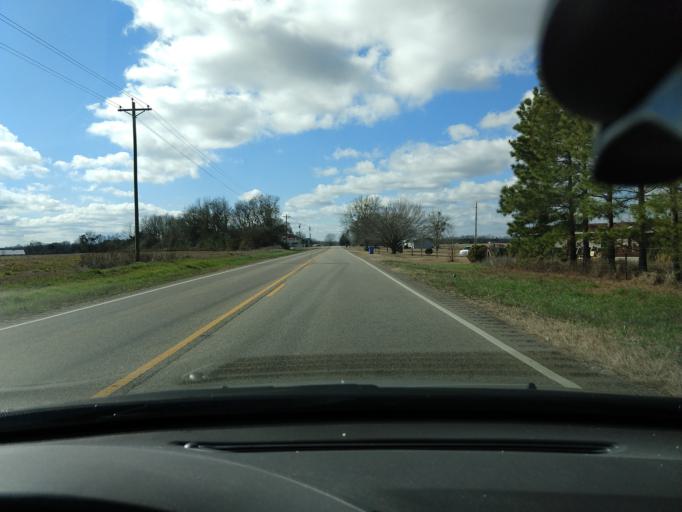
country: US
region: Alabama
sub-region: Coffee County
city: Elba
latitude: 31.3106
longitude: -86.0338
